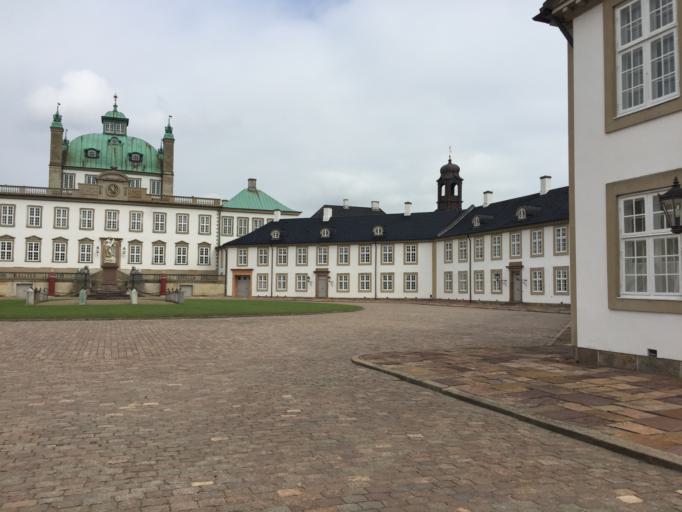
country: DK
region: Capital Region
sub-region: Fredensborg Kommune
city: Fredensborg
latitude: 55.9816
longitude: 12.3958
